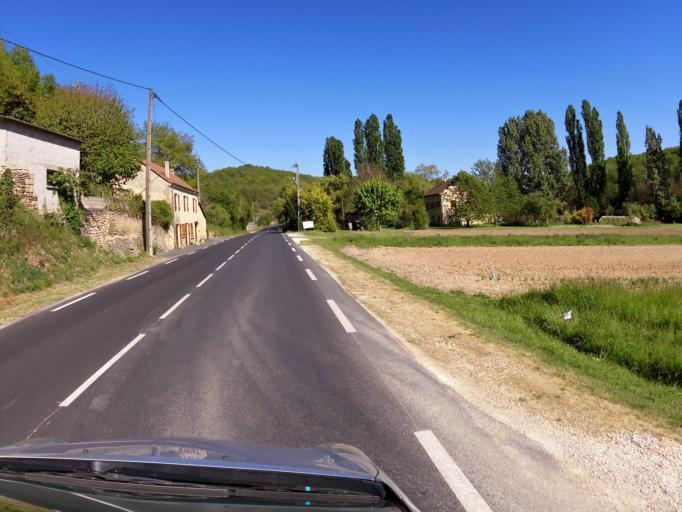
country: FR
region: Aquitaine
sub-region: Departement de la Dordogne
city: Montignac
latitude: 45.0619
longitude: 1.1878
